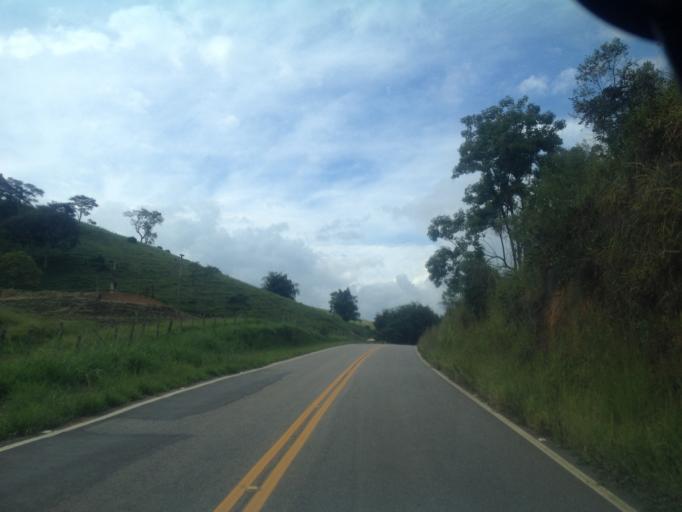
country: BR
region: Rio de Janeiro
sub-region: Quatis
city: Quatis
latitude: -22.3562
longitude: -44.2523
